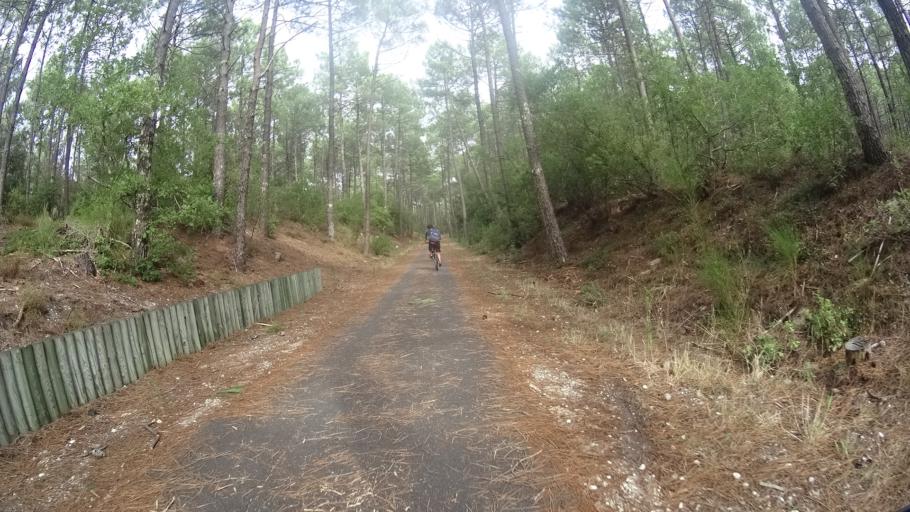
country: FR
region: Aquitaine
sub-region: Departement de la Gironde
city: Lacanau
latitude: 45.0074
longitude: -1.1491
